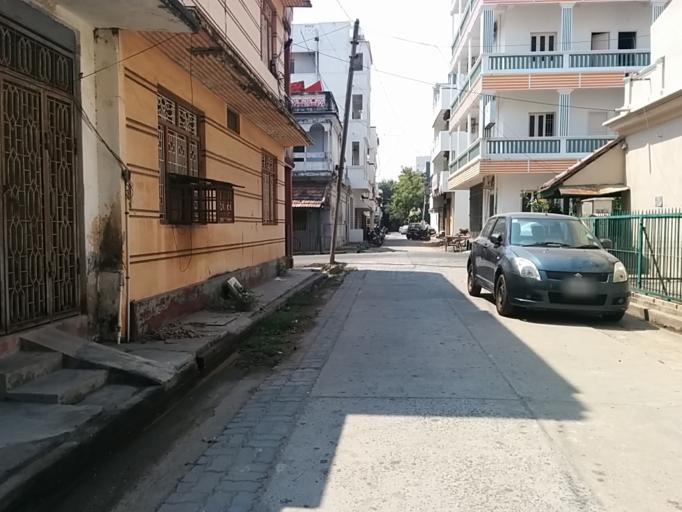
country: IN
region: Pondicherry
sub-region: Puducherry
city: Puducherry
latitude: 11.9399
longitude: 79.8325
